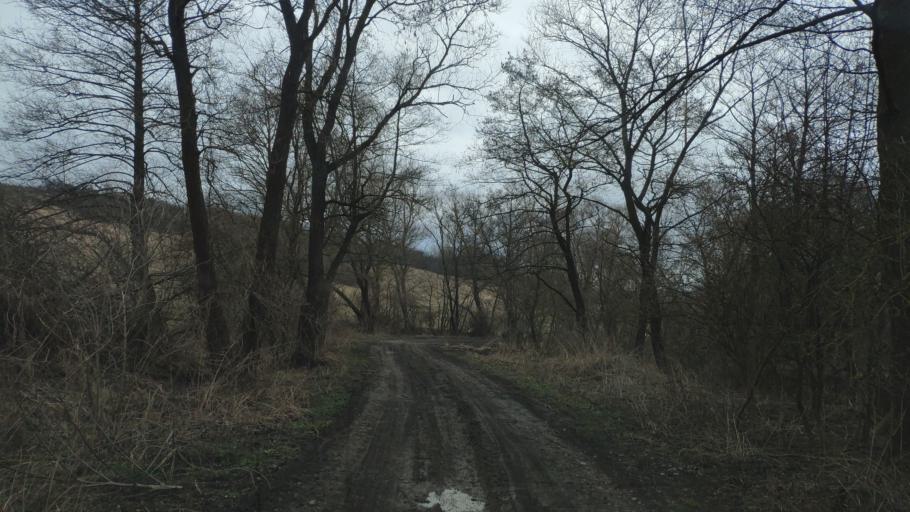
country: SK
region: Presovsky
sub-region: Okres Presov
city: Presov
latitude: 49.0759
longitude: 21.2964
